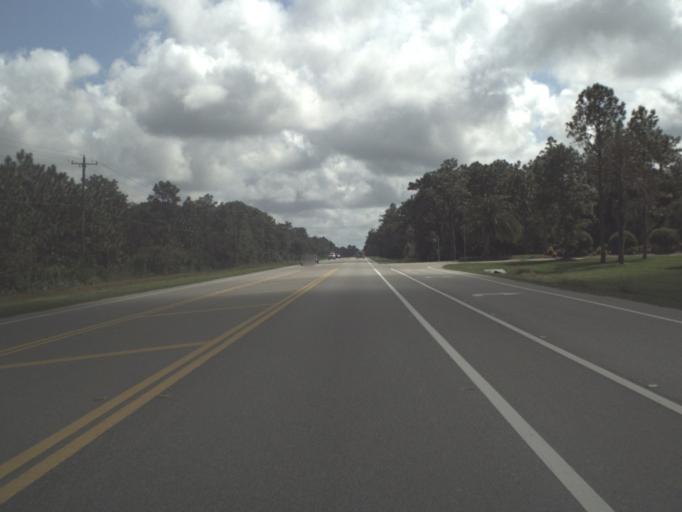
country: US
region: Florida
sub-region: Sarasota County
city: The Meadows
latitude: 27.4068
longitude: -82.3257
